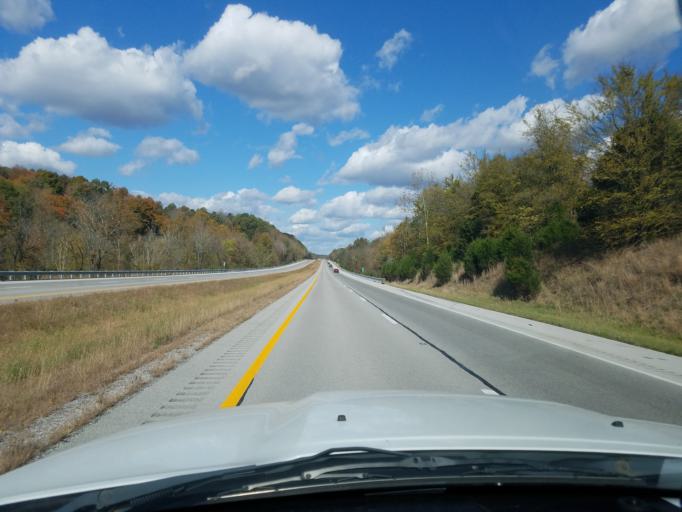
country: US
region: Kentucky
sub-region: Butler County
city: Morgantown
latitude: 37.1486
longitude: -86.6551
